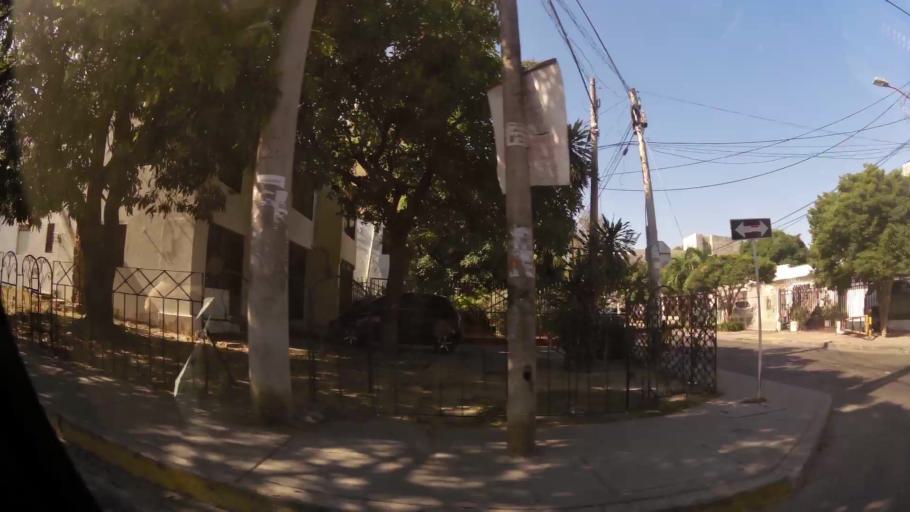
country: CO
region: Bolivar
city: Cartagena
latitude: 10.3922
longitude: -75.4750
